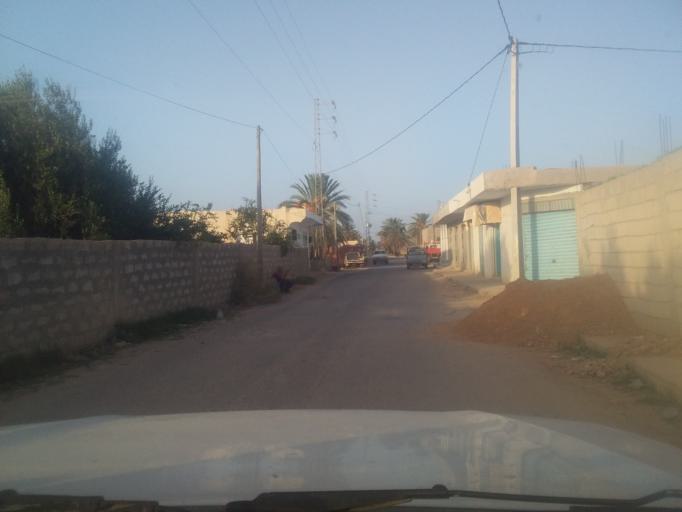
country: TN
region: Qabis
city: Gabes
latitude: 33.6223
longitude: 10.2935
